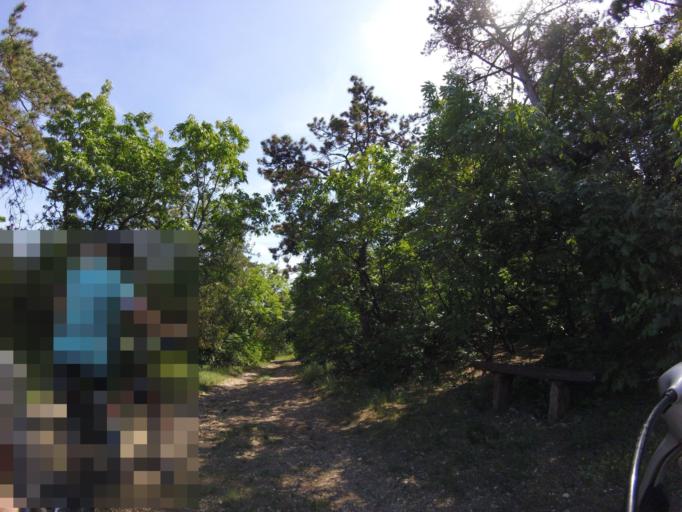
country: HU
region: Fejer
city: Kincsesbanya
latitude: 47.2371
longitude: 18.2880
